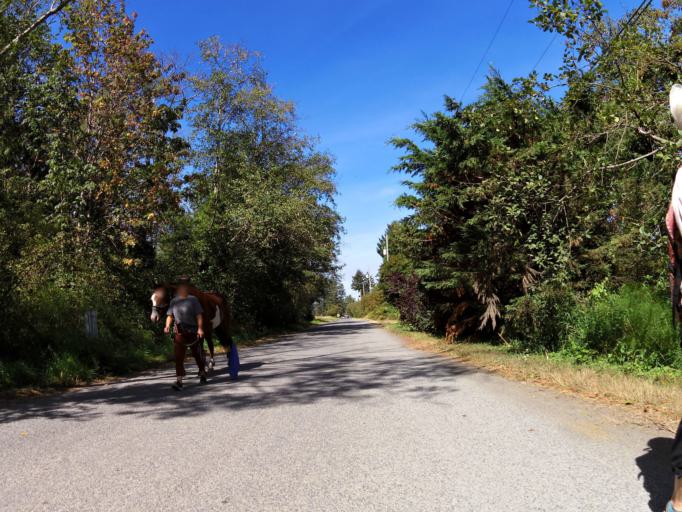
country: CA
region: British Columbia
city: North Saanich
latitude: 48.5593
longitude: -123.3880
